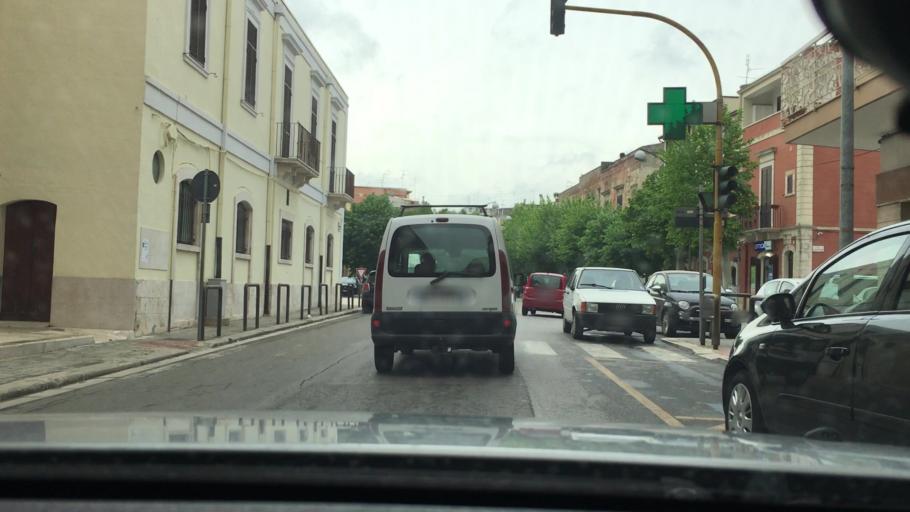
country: IT
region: Apulia
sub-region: Provincia di Bari
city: Gioia del Colle
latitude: 40.8040
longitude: 16.9235
